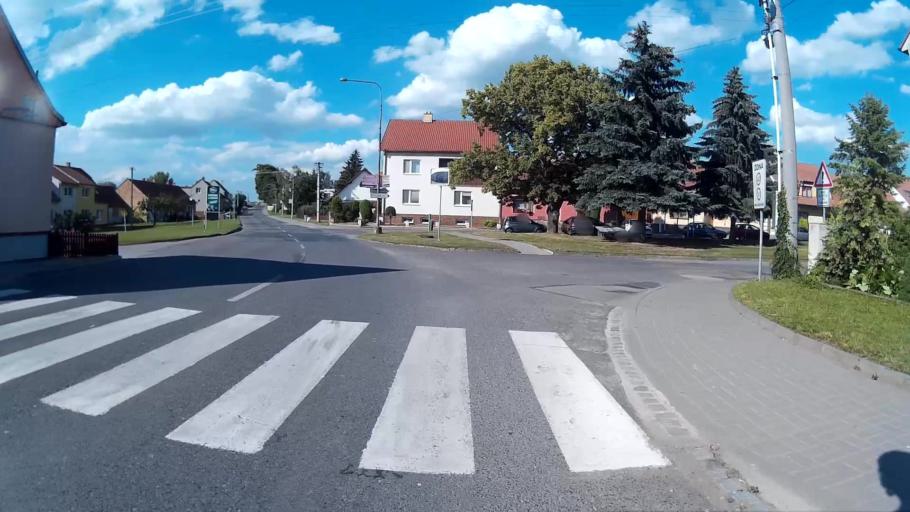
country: CZ
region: South Moravian
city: Sitborice
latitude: 49.0166
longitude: 16.7757
